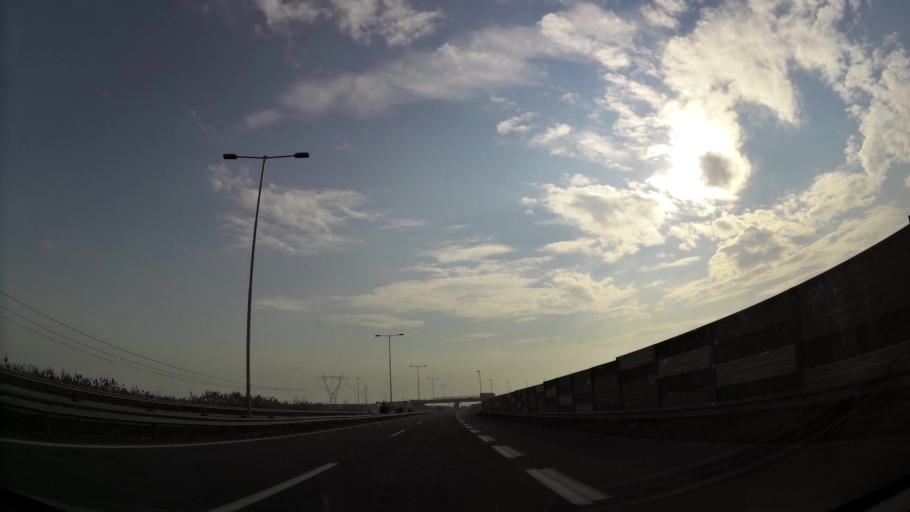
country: MK
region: Aracinovo
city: Arachinovo
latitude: 42.0206
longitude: 21.5331
